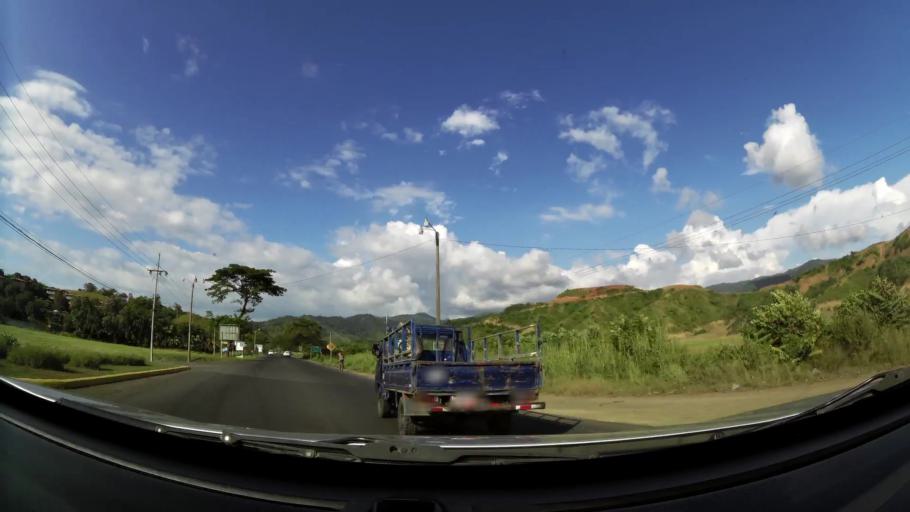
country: CR
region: Puntarenas
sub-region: Canton de Garabito
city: Jaco
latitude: 9.6354
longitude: -84.6275
